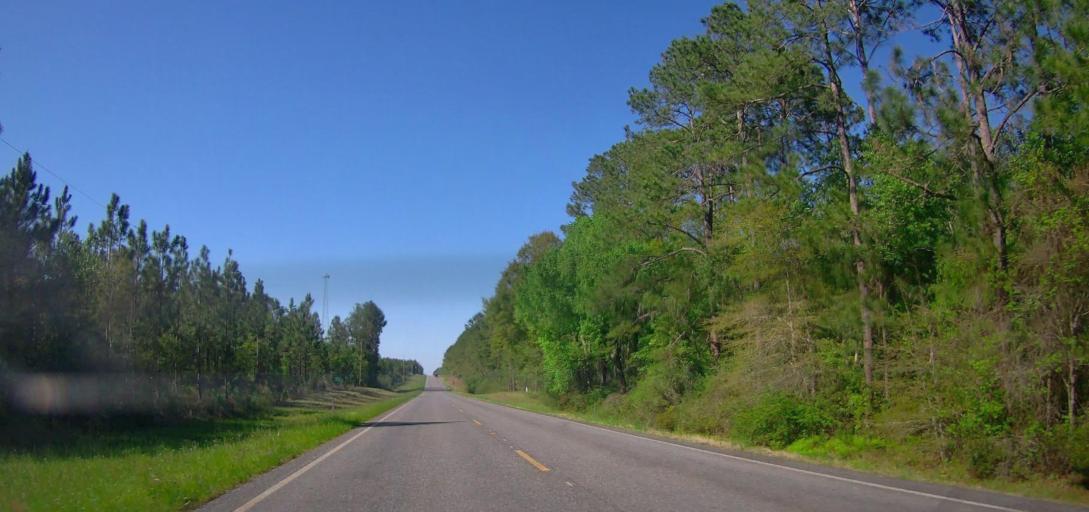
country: US
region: Georgia
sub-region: Wilcox County
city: Rochelle
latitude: 32.0384
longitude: -83.5038
